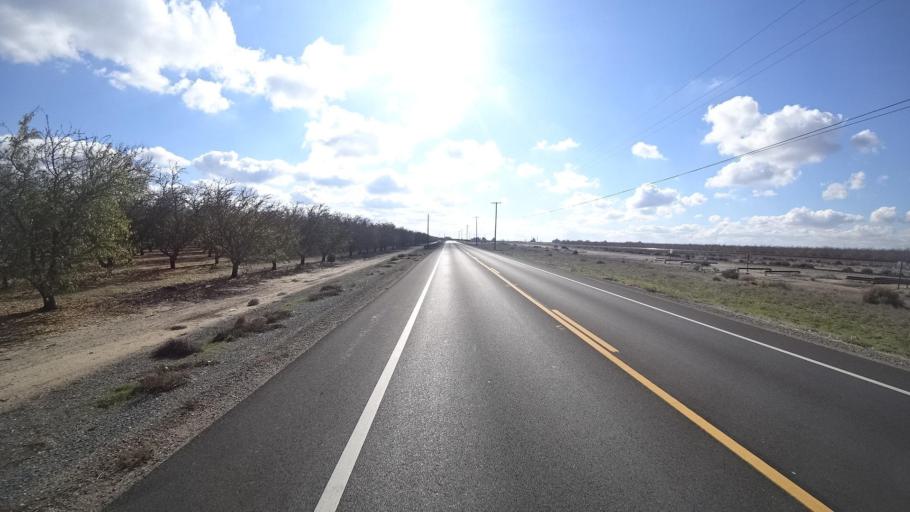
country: US
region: California
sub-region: Kern County
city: Wasco
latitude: 35.6790
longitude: -119.3300
